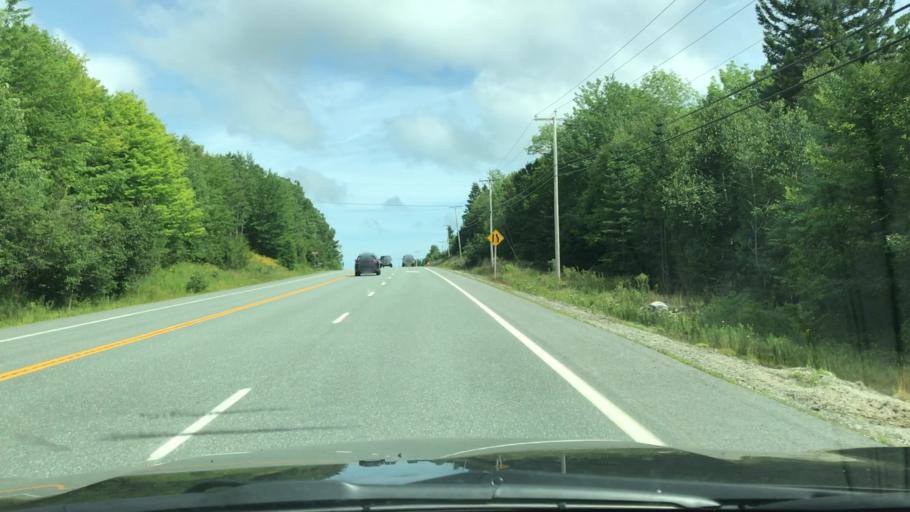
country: US
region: Maine
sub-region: Hancock County
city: Surry
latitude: 44.5475
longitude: -68.5240
